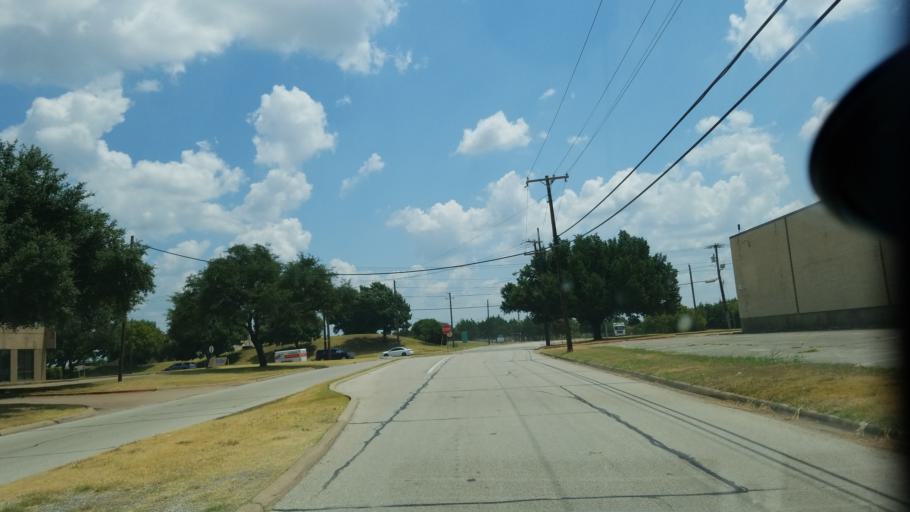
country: US
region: Texas
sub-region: Dallas County
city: Duncanville
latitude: 32.6872
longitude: -96.8837
